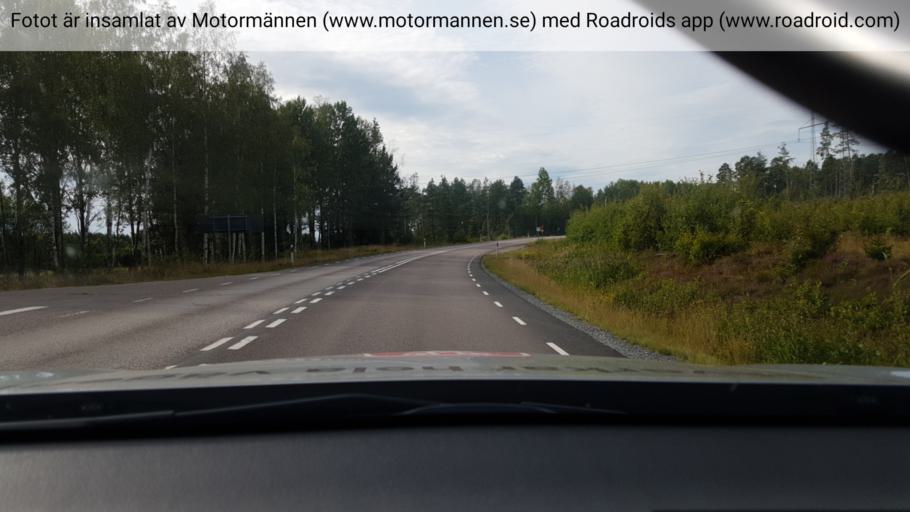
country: SE
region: Vaestra Goetaland
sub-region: Amals Kommun
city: Amal
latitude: 59.0581
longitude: 12.6565
